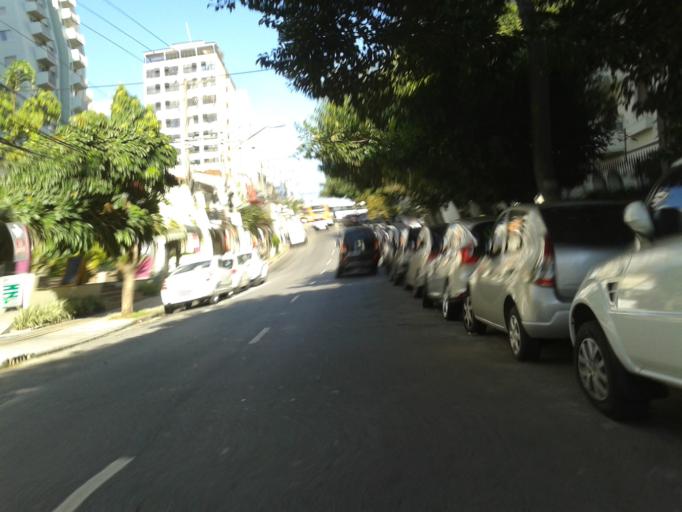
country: BR
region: Sao Paulo
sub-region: Sao Paulo
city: Sao Paulo
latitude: -23.5552
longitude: -46.6756
